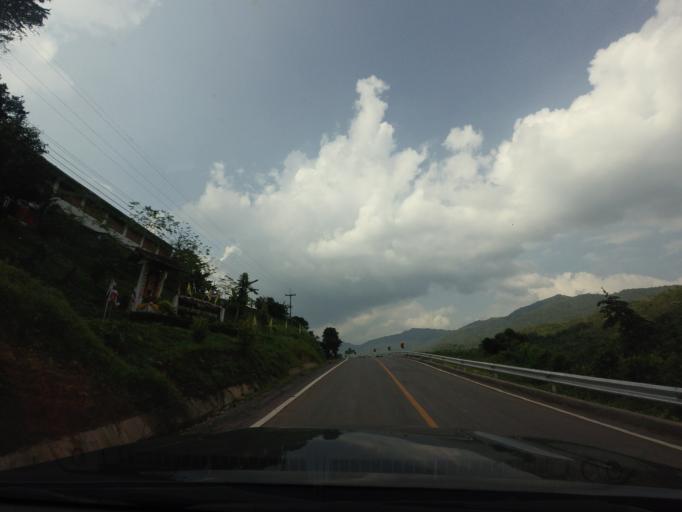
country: TH
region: Nan
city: Bo Kluea
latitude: 19.2085
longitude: 101.1857
